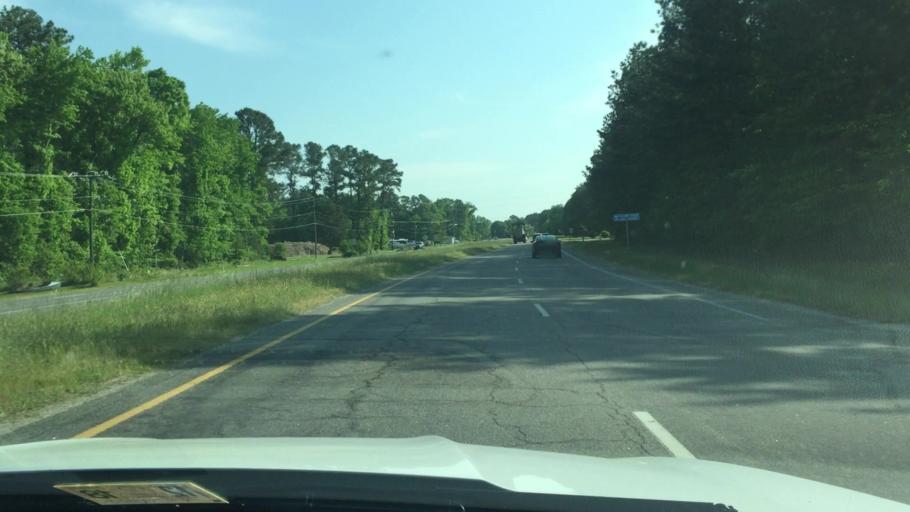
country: US
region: Virginia
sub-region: Lancaster County
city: Kilmarnock
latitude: 37.6603
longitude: -76.3871
